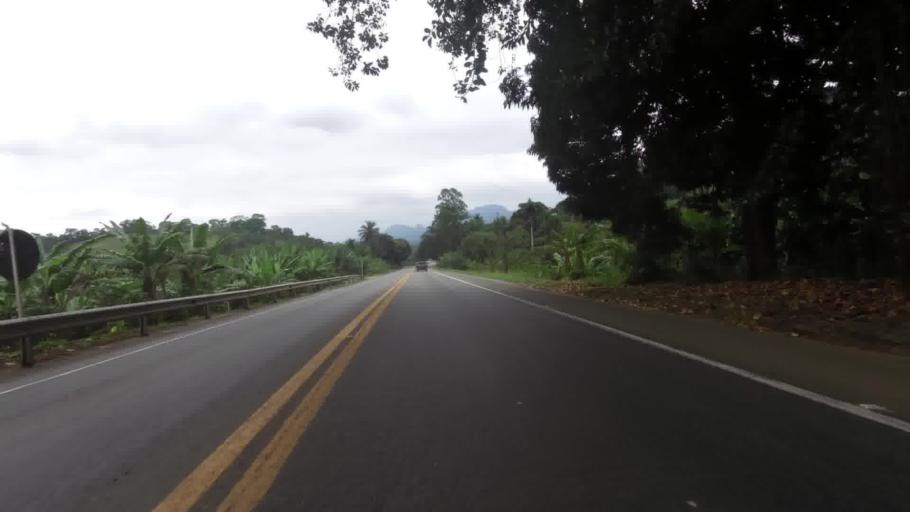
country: BR
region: Espirito Santo
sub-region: Iconha
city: Iconha
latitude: -20.7875
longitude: -40.7846
